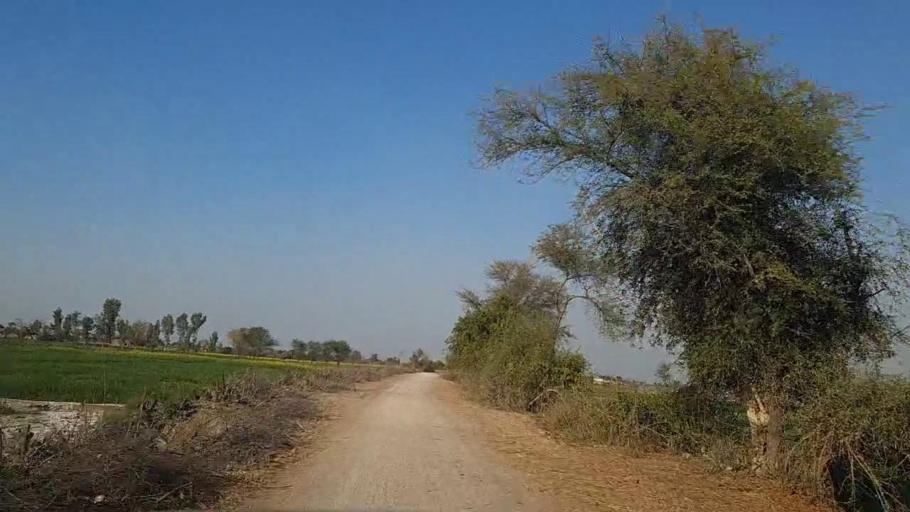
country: PK
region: Sindh
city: Daur
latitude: 26.3190
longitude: 68.1780
